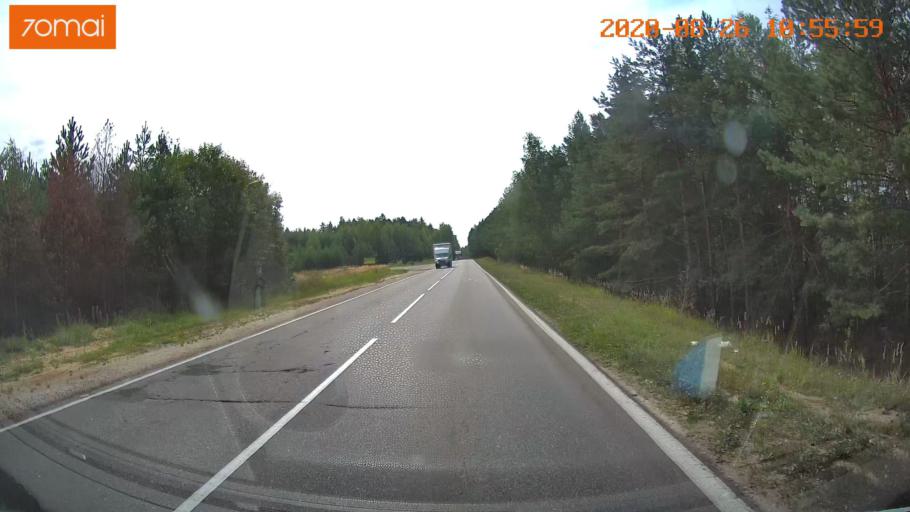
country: RU
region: Rjazan
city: Izhevskoye
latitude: 54.6095
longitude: 41.1832
